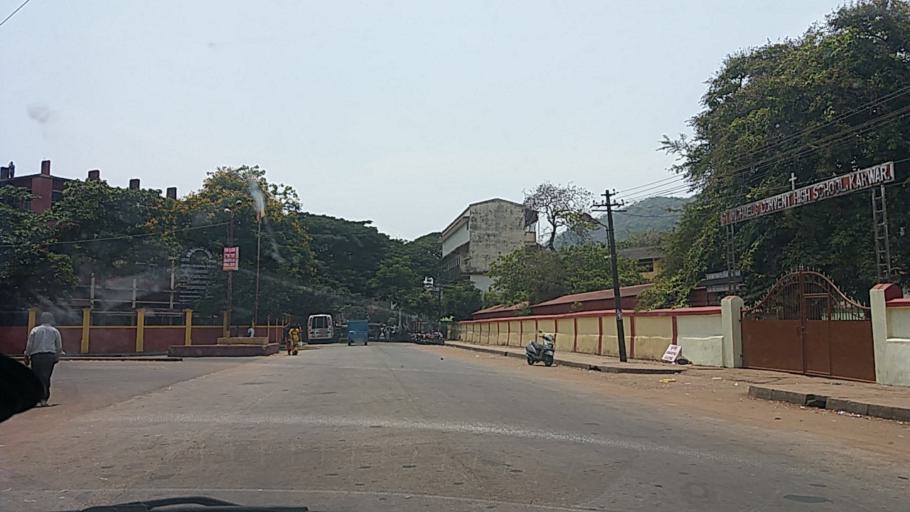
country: IN
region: Karnataka
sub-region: Uttar Kannada
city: Karwar
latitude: 14.8065
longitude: 74.1266
